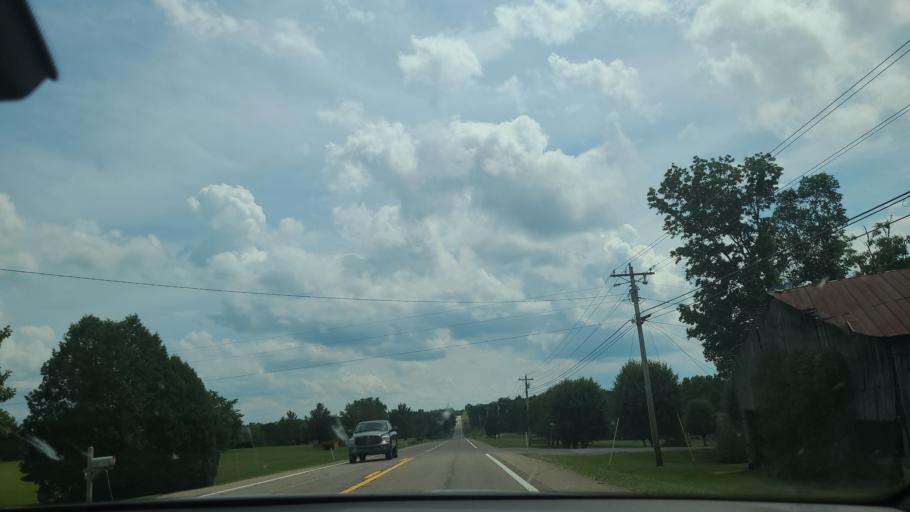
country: US
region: Tennessee
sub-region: Cumberland County
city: Lake Tansi
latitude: 35.8569
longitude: -85.0101
